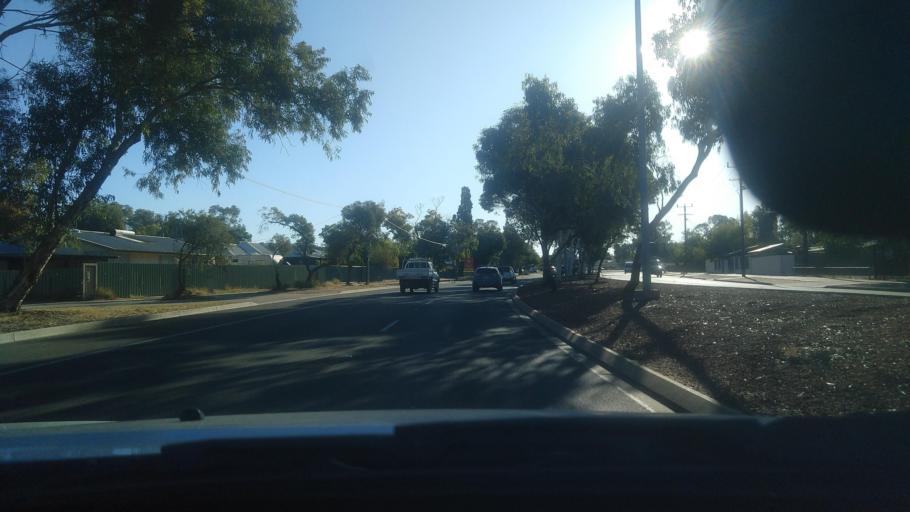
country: AU
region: Northern Territory
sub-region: Alice Springs
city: Alice Springs
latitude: -23.7016
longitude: 133.8707
